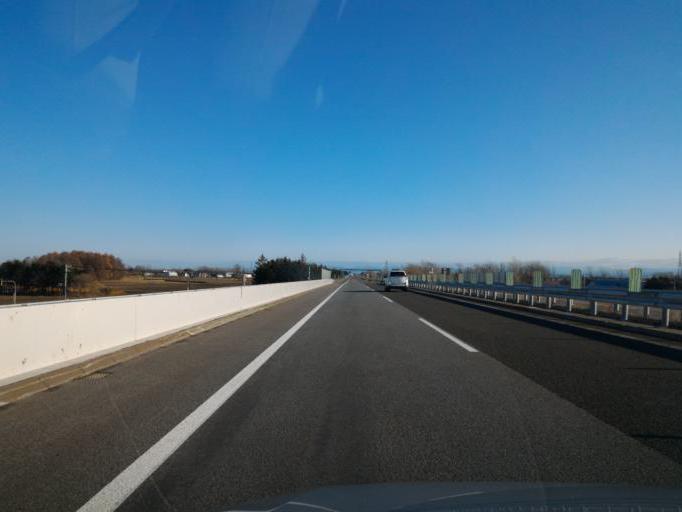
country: JP
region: Hokkaido
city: Ebetsu
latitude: 43.0957
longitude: 141.5821
